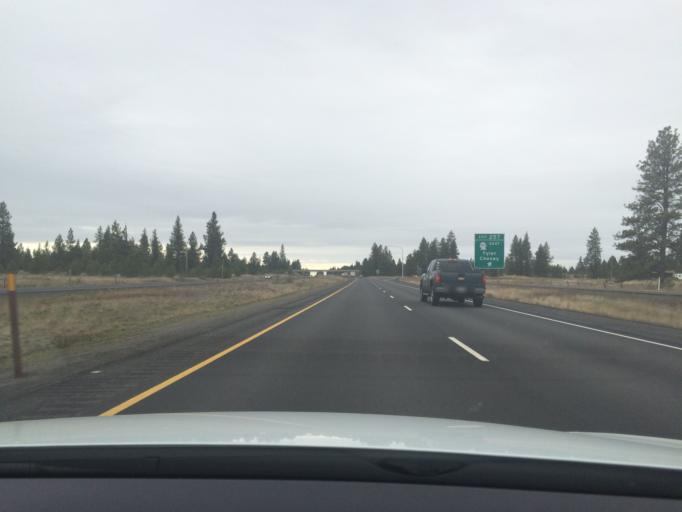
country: US
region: Washington
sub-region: Spokane County
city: Medical Lake
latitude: 47.4405
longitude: -117.7850
